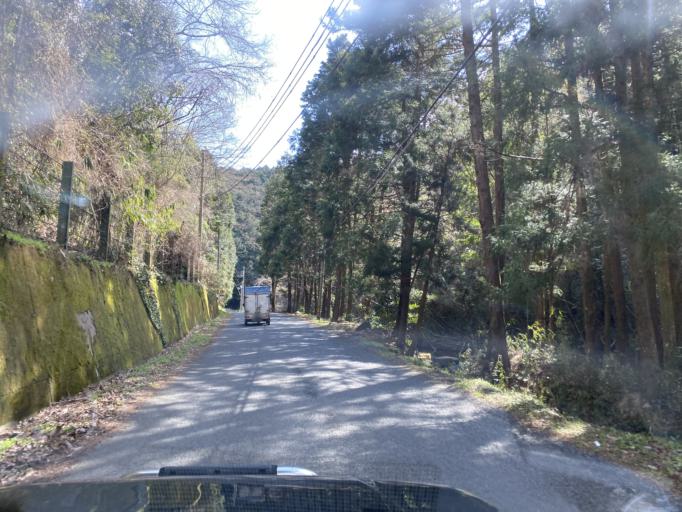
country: JP
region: Nara
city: Nara-shi
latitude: 34.7047
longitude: 135.9494
